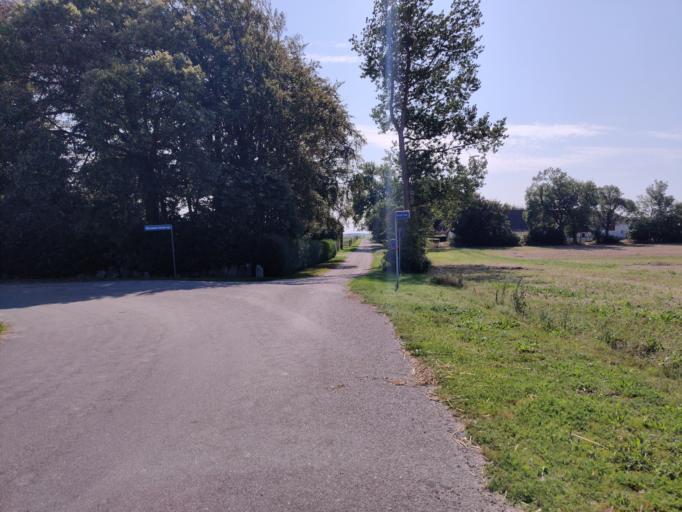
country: DK
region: Zealand
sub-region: Guldborgsund Kommune
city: Nykobing Falster
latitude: 54.6778
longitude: 11.8904
